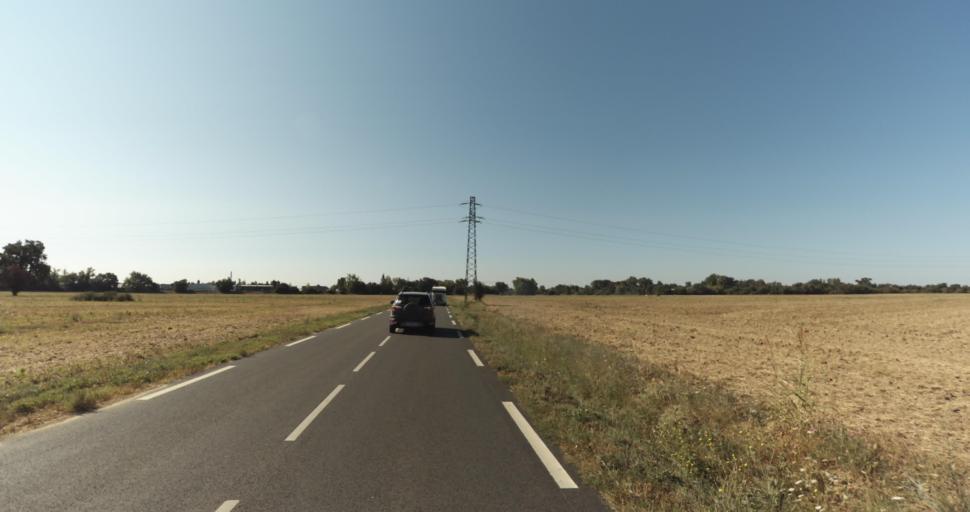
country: FR
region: Midi-Pyrenees
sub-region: Departement de la Haute-Garonne
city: Launaguet
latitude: 43.6676
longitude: 1.4583
